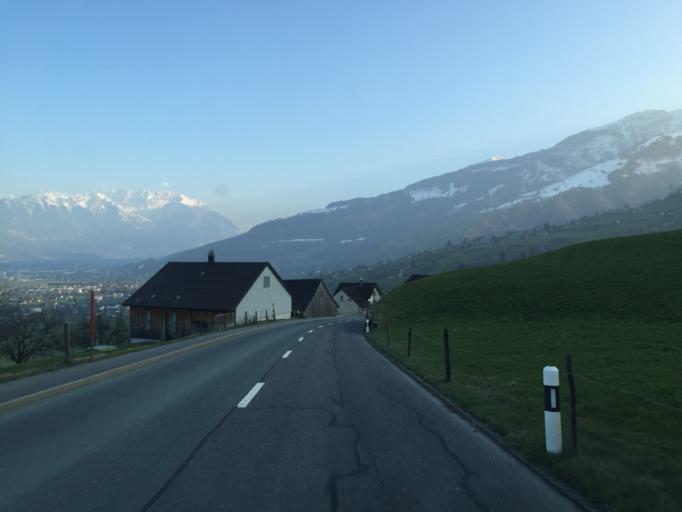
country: CH
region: Saint Gallen
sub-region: Wahlkreis Werdenberg
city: Gams
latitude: 47.1996
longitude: 9.4319
